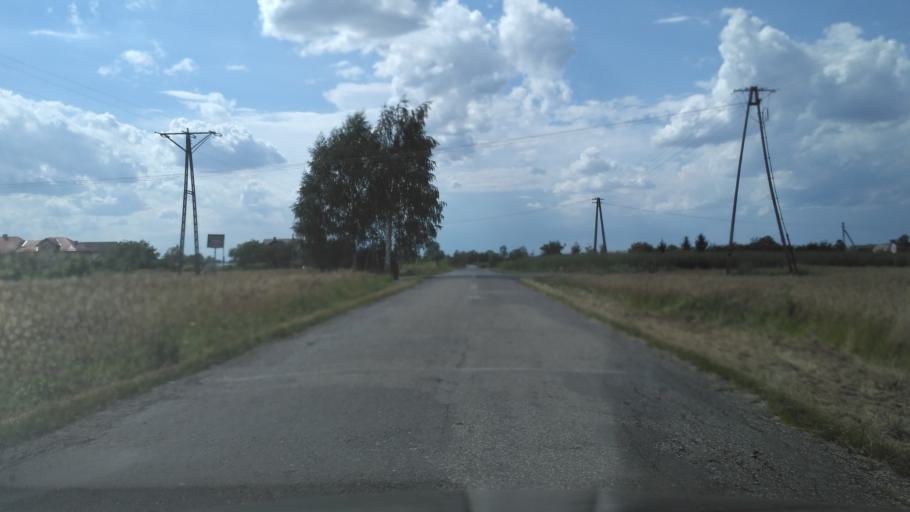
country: PL
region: Lublin Voivodeship
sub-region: Powiat leczynski
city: Milejow
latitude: 51.2163
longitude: 22.9088
